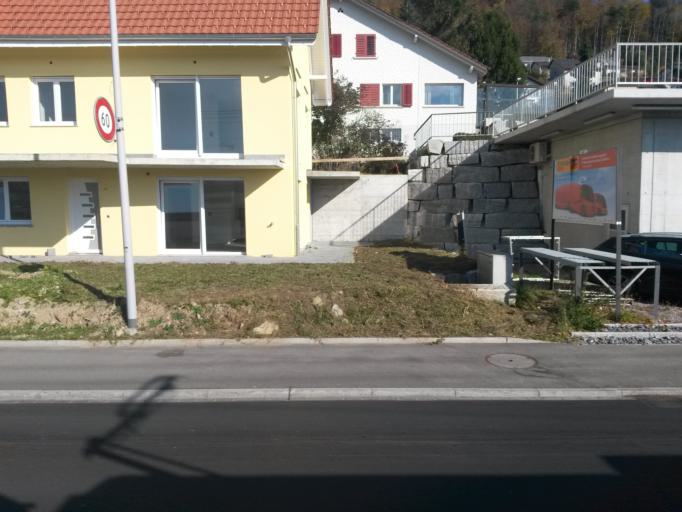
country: CH
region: Aargau
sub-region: Bezirk Kulm
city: Gontenschwil
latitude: 47.2736
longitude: 8.1670
